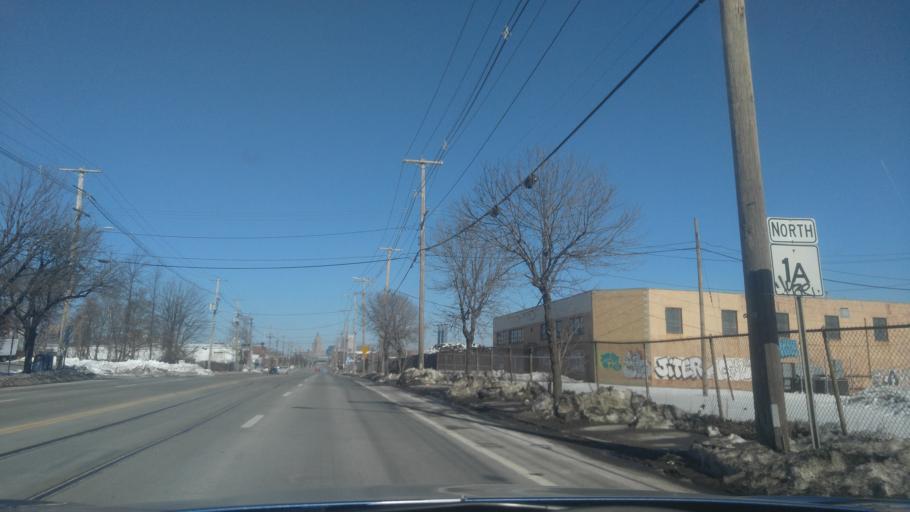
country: US
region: Rhode Island
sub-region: Providence County
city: Providence
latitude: 41.8026
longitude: -71.4012
